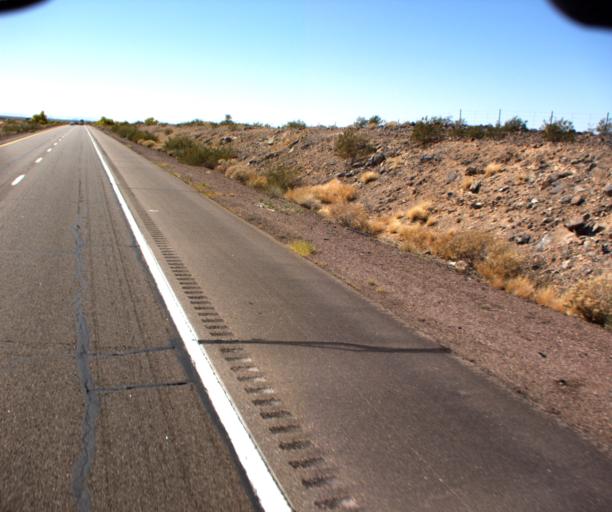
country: US
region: Arizona
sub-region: Maricopa County
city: Gila Bend
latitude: 32.8716
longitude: -113.1362
